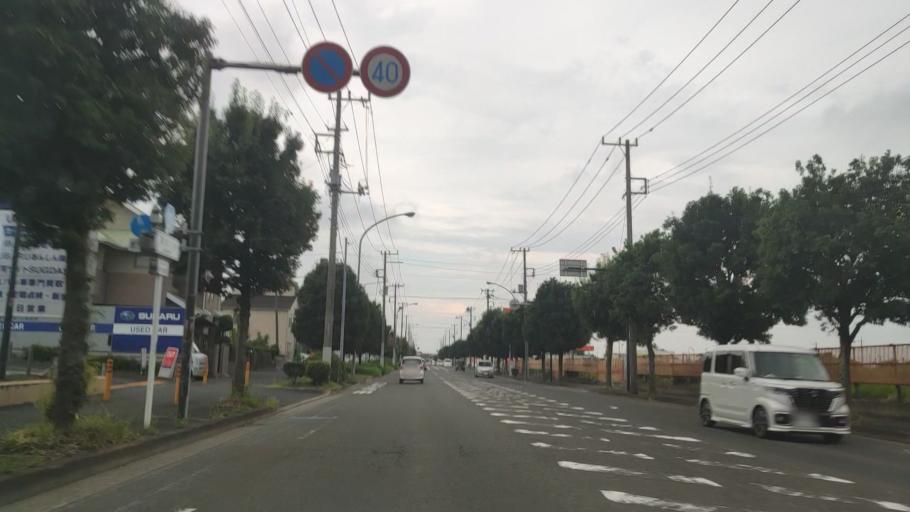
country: JP
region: Kanagawa
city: Fujisawa
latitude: 35.4069
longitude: 139.4841
